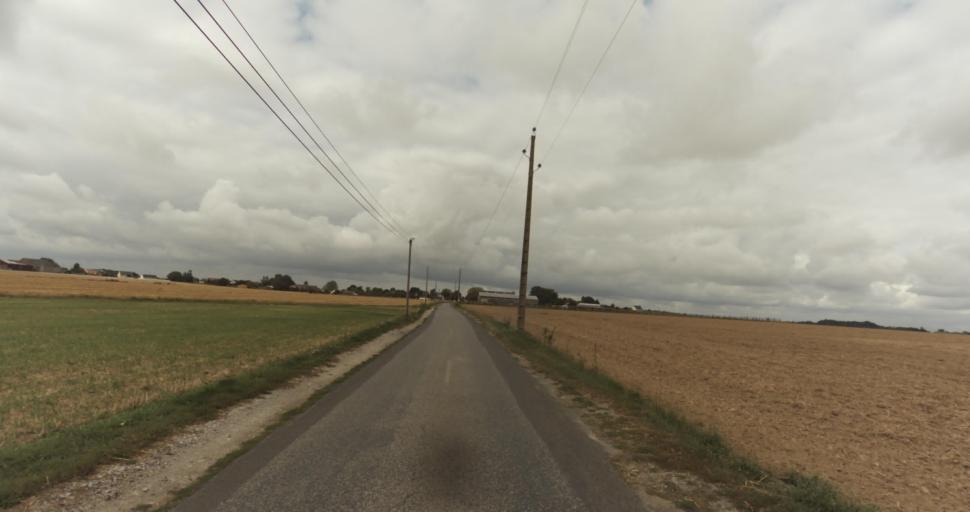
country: FR
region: Haute-Normandie
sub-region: Departement de l'Eure
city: La Couture-Boussey
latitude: 48.9310
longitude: 1.3312
